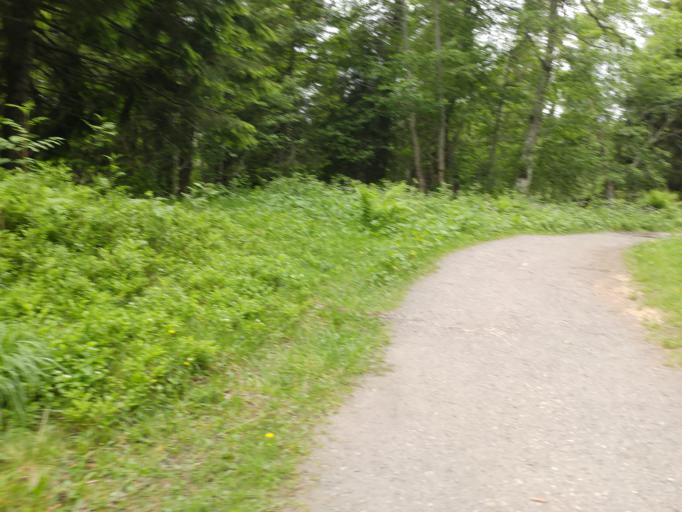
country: NO
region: Sor-Trondelag
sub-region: Melhus
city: Melhus
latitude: 63.4004
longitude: 10.2631
